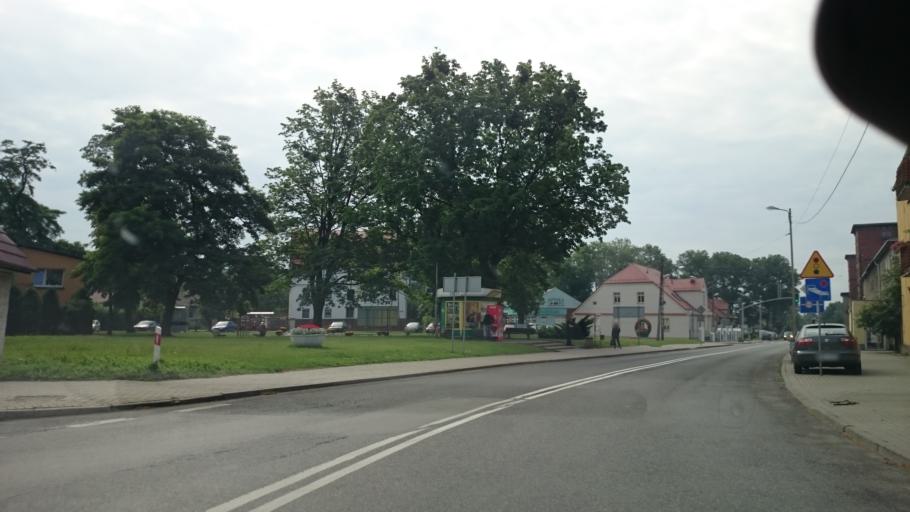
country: PL
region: Silesian Voivodeship
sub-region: Powiat gliwicki
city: Toszek
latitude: 50.4544
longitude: 18.5220
